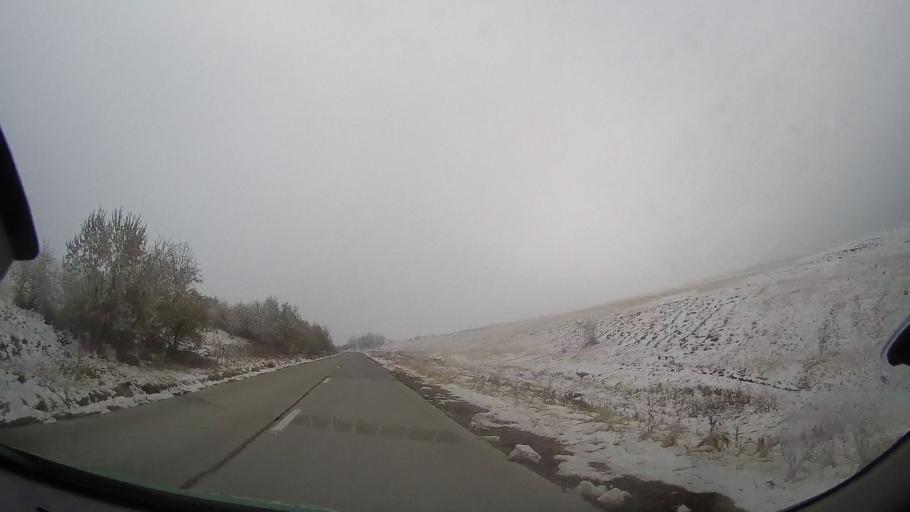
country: RO
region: Vaslui
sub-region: Comuna Ivesti
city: Ivesti
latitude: 46.2082
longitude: 27.5047
